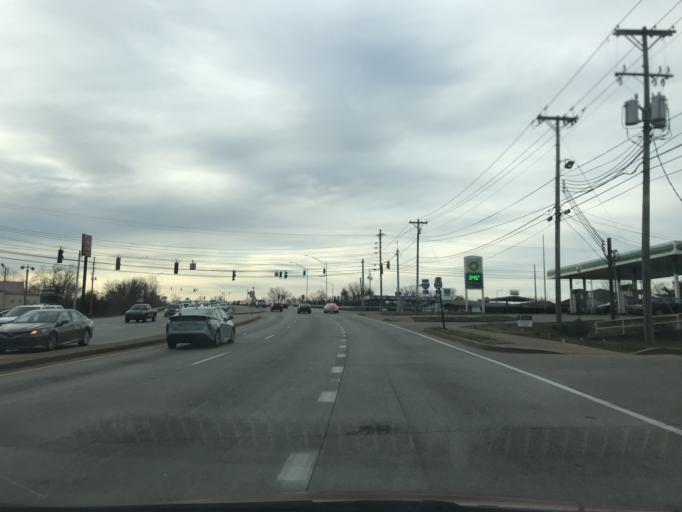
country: US
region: Kentucky
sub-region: Jefferson County
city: West Buechel
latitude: 38.2004
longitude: -85.6852
